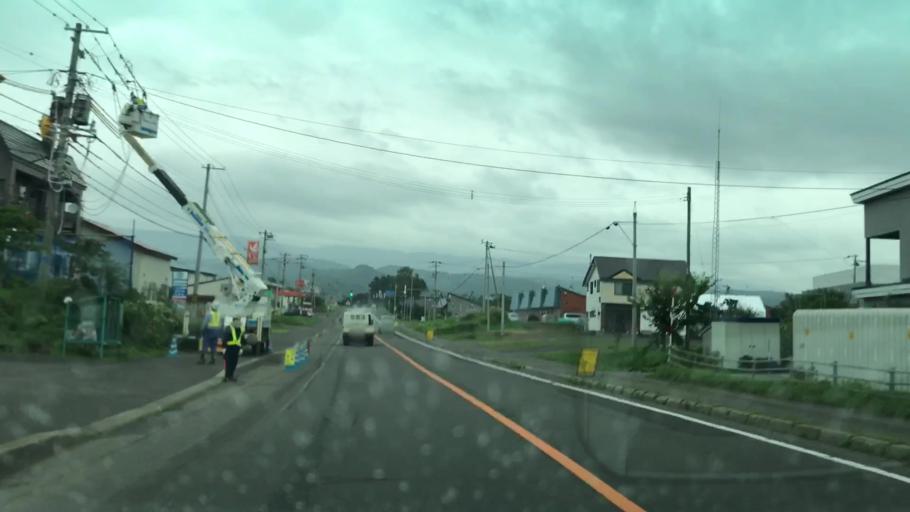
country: JP
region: Hokkaido
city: Niseko Town
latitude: 42.8102
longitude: 140.5413
